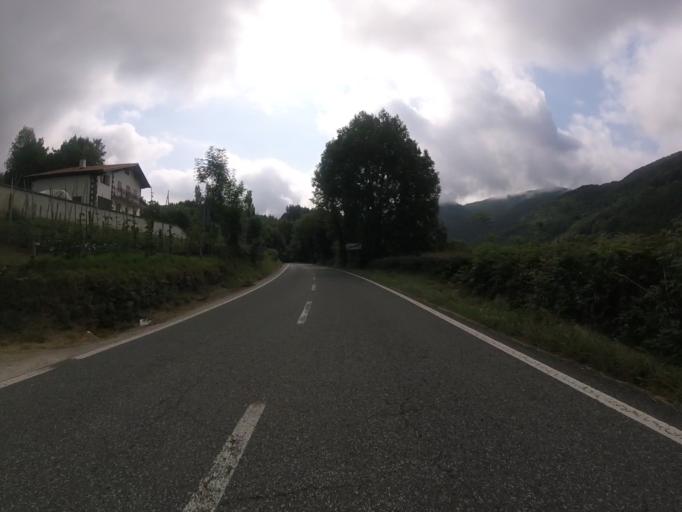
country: ES
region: Navarre
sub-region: Provincia de Navarra
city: Ezkurra
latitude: 43.0845
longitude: -1.8228
